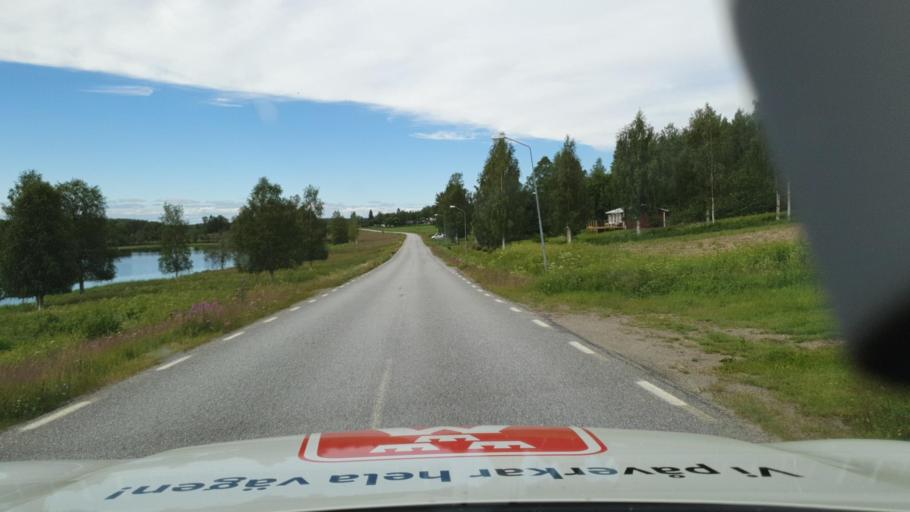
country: SE
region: Vaesterbotten
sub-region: Skelleftea Kommun
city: Burea
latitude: 64.4950
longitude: 21.0210
